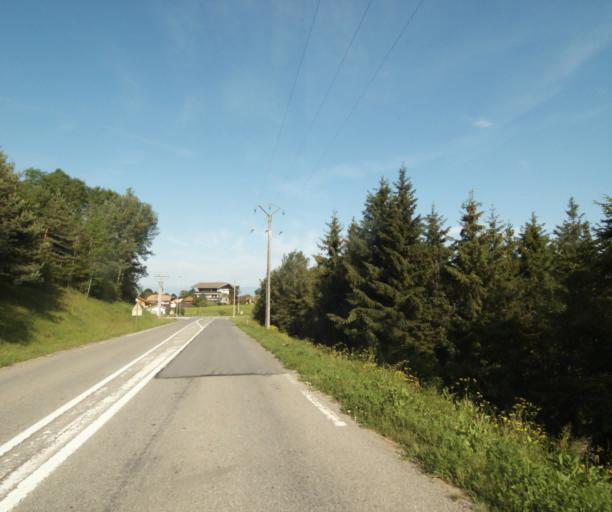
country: FR
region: Rhone-Alpes
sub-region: Departement de la Haute-Savoie
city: Armoy
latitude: 46.3464
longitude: 6.5253
